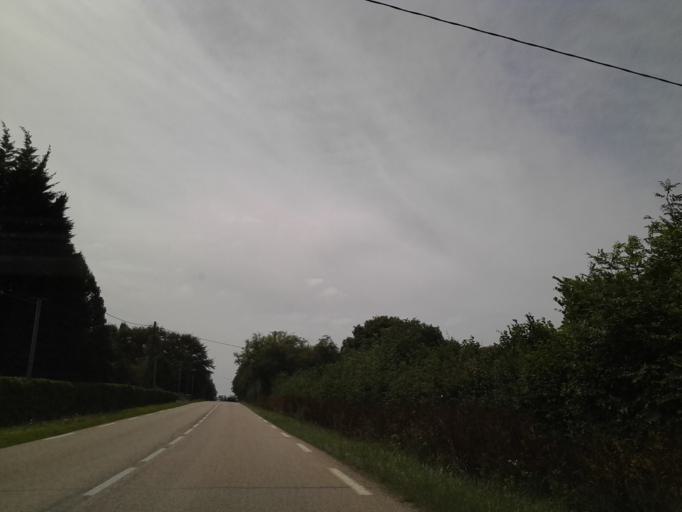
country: FR
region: Lower Normandy
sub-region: Departement de la Manche
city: Sottevast
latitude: 49.4941
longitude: -1.5379
